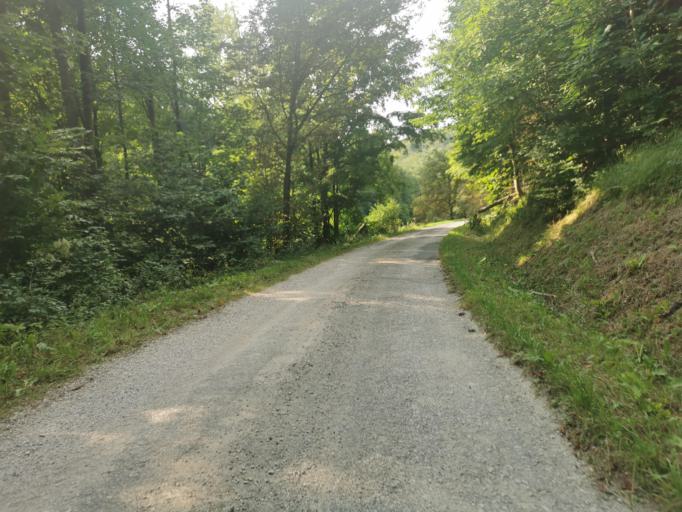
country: SK
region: Nitriansky
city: Stara Tura
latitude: 48.8175
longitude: 17.6324
